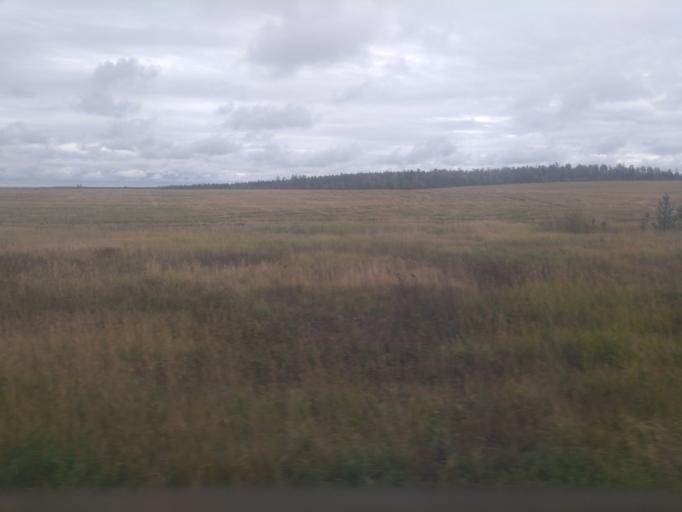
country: RU
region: Udmurtiya
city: Alnashi
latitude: 56.1379
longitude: 52.5664
